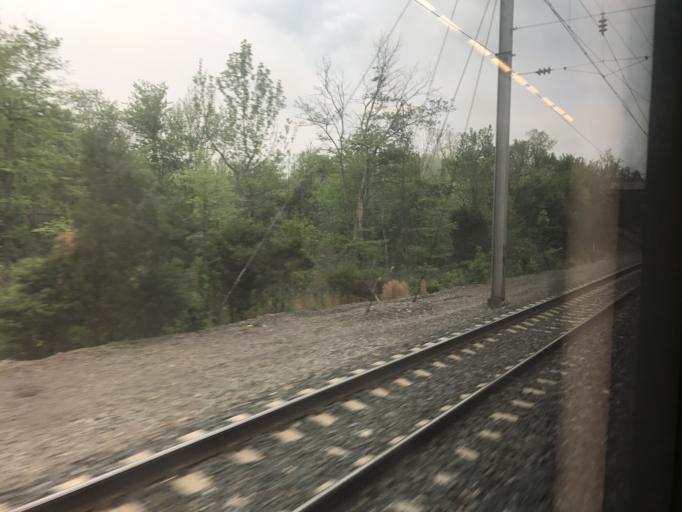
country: US
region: Maryland
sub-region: Prince George's County
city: Glenn Dale
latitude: 38.9880
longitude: -76.8151
